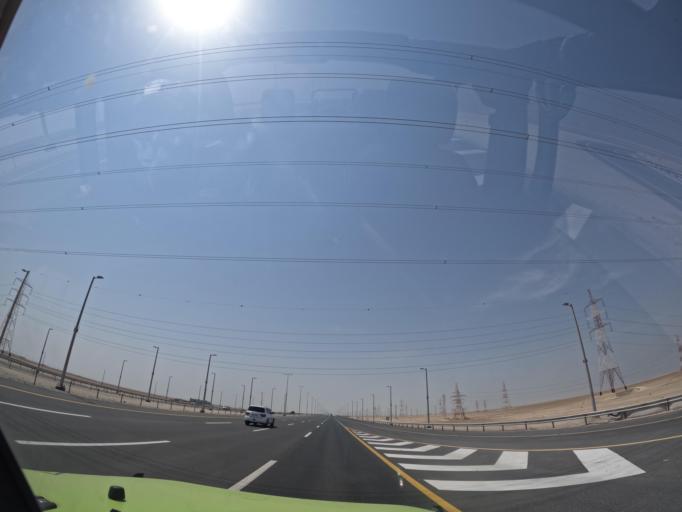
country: AE
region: Abu Dhabi
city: Abu Dhabi
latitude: 24.1561
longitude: 54.3050
